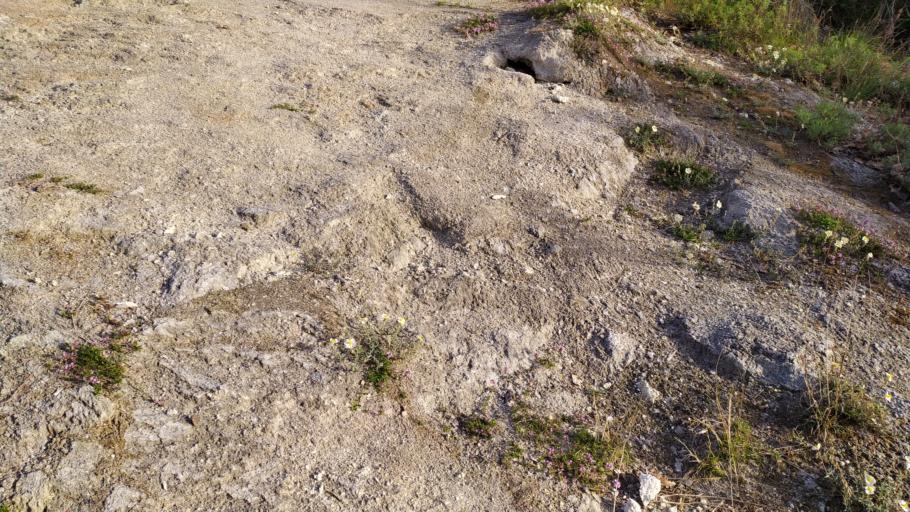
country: IT
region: Emilia-Romagna
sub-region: Provincia di Ravenna
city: Fognano
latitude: 44.2281
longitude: 11.7380
